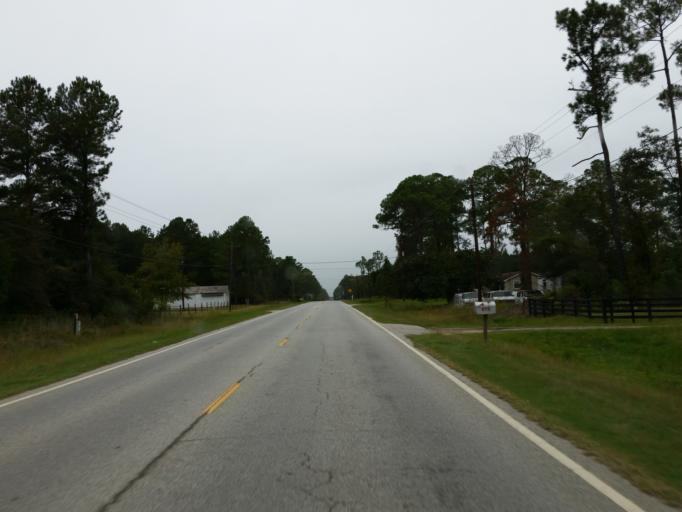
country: US
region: Georgia
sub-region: Lanier County
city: Lakeland
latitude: 31.0431
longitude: -83.0985
